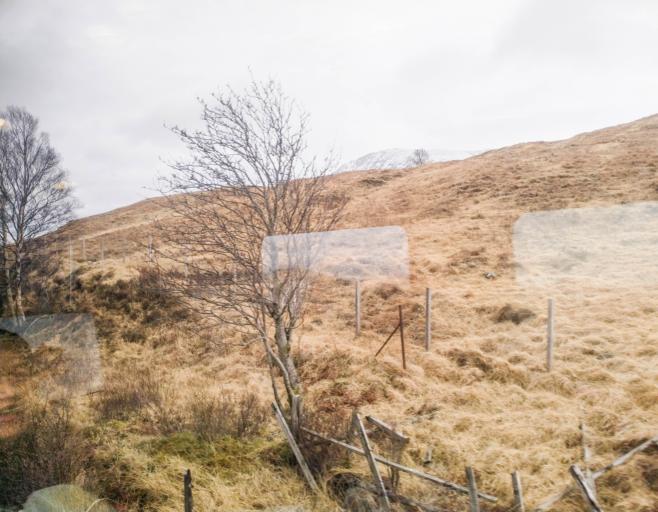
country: GB
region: Scotland
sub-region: Highland
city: Spean Bridge
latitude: 56.5475
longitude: -4.7528
